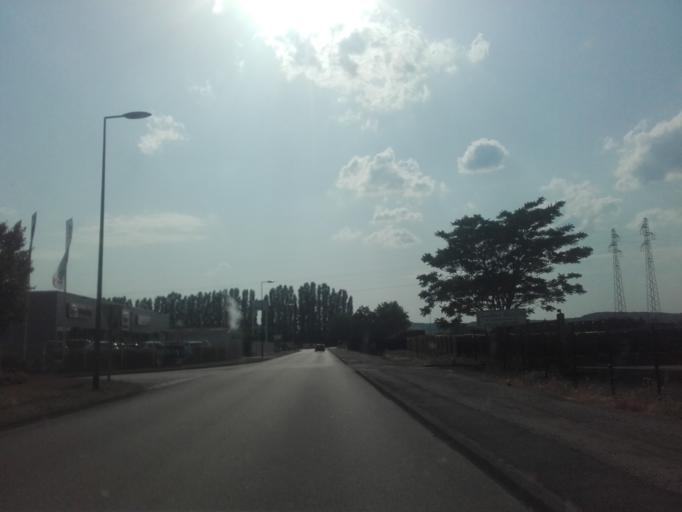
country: FR
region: Bourgogne
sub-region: Departement de la Cote-d'Or
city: Beaune
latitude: 47.0239
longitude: 4.8619
